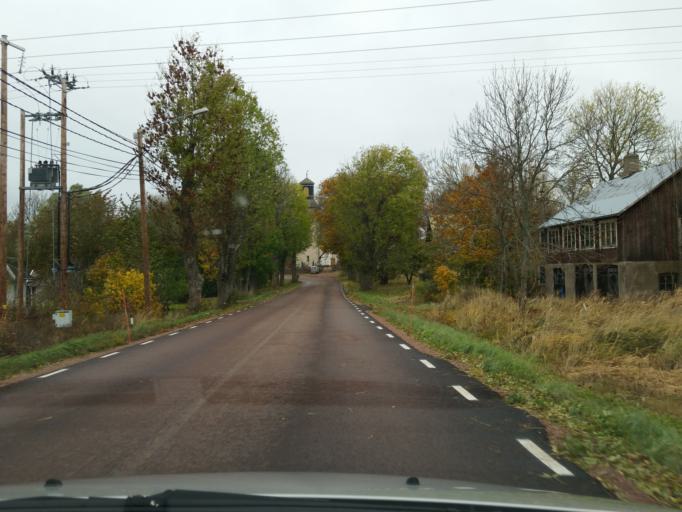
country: AX
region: Alands landsbygd
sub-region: Lemland
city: Lemland
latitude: 60.0727
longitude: 20.0846
